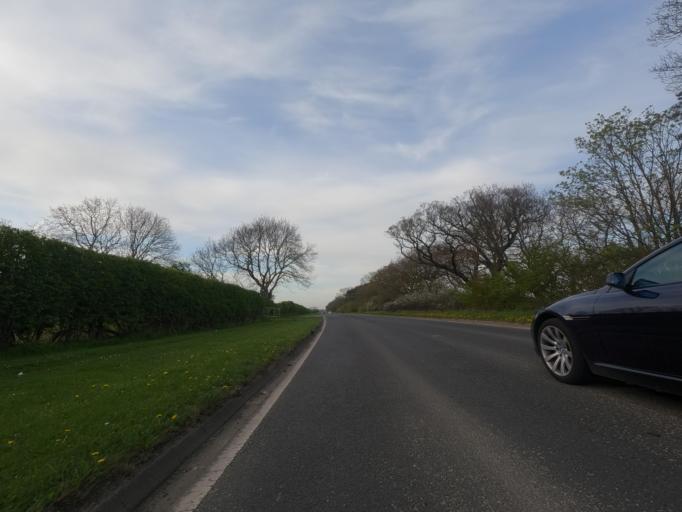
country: GB
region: England
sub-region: Newcastle upon Tyne
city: Dinnington
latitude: 55.0359
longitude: -1.6653
